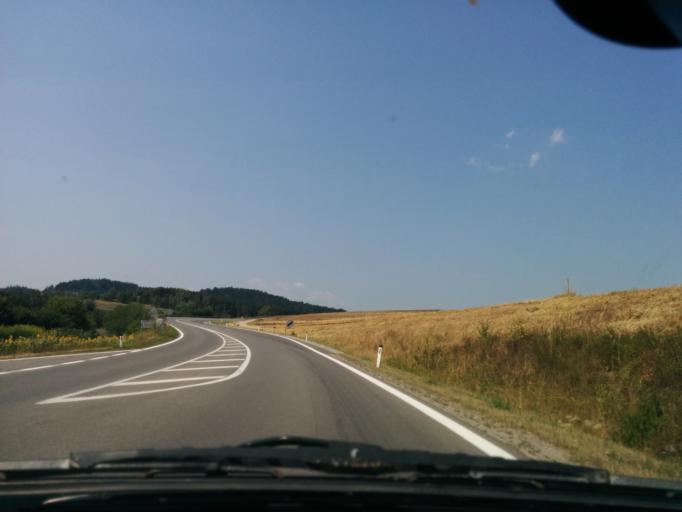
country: AT
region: Lower Austria
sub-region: Politischer Bezirk Krems
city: Rastenfeld
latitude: 48.5454
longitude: 15.3653
